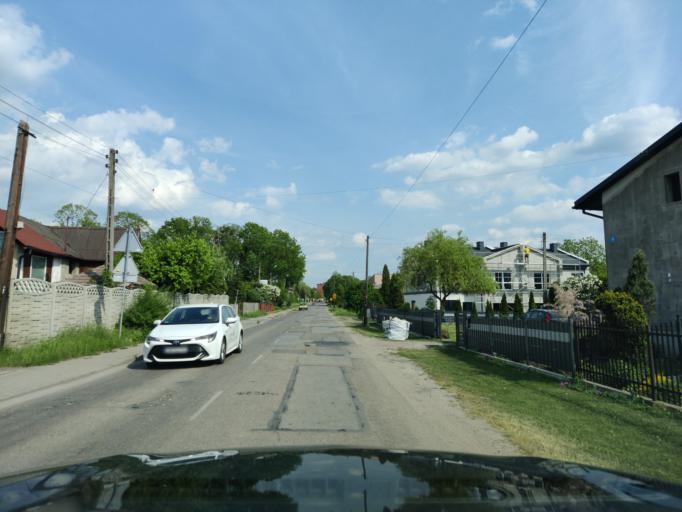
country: PL
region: Silesian Voivodeship
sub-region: Powiat bedzinski
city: Siewierz
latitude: 50.3977
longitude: 19.2370
